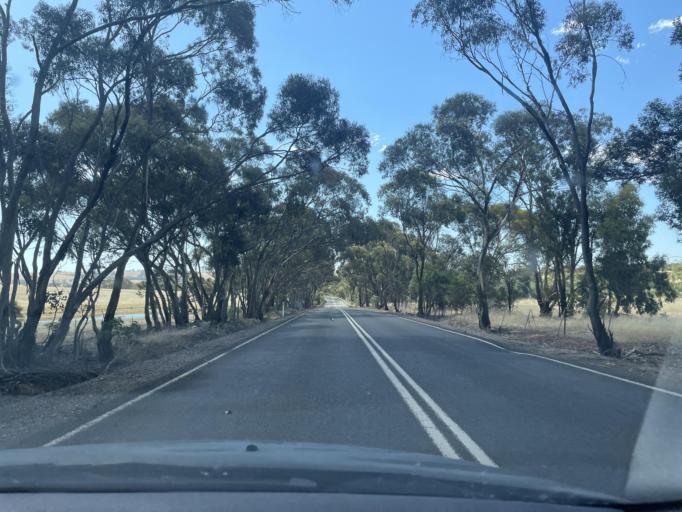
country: AU
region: South Australia
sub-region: Clare and Gilbert Valleys
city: Clare
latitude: -33.9031
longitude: 138.6932
